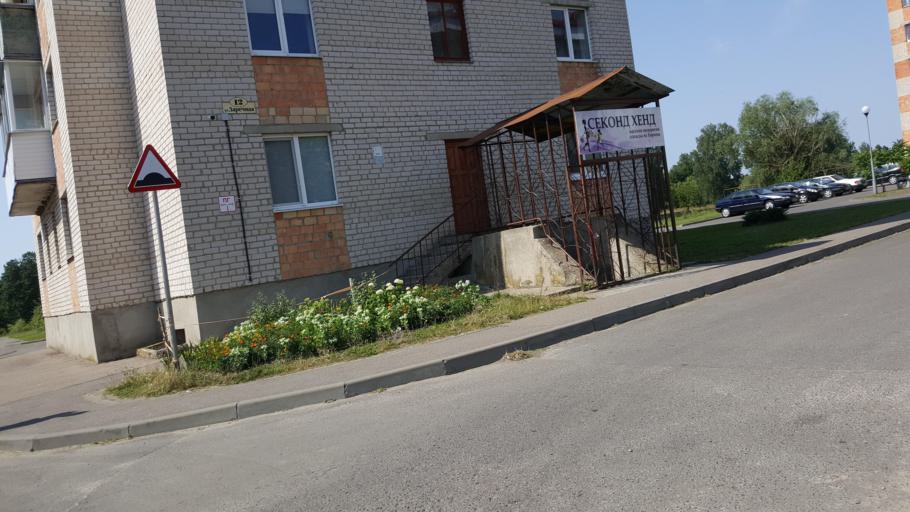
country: BY
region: Brest
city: Zhabinka
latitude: 52.1930
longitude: 24.0297
